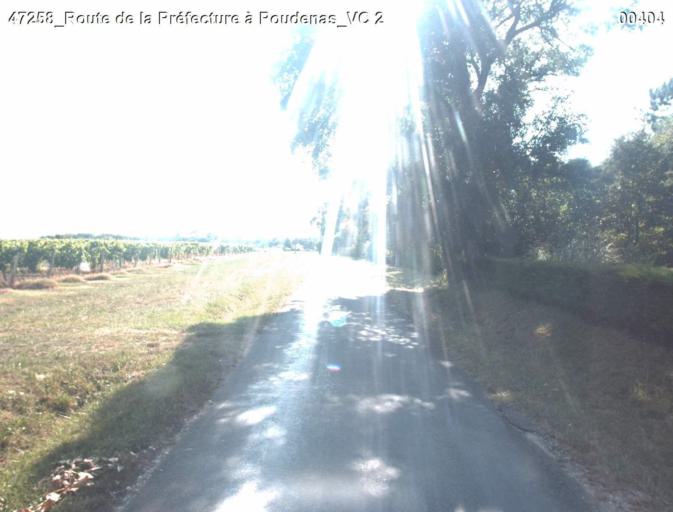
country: FR
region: Midi-Pyrenees
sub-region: Departement du Gers
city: Montreal
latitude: 44.0184
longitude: 0.1650
